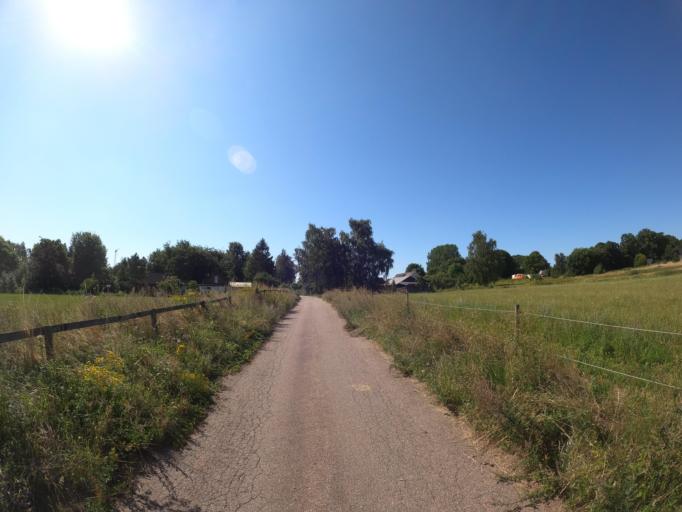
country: SE
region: Skane
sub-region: Lunds Kommun
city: Veberod
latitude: 55.6779
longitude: 13.4251
